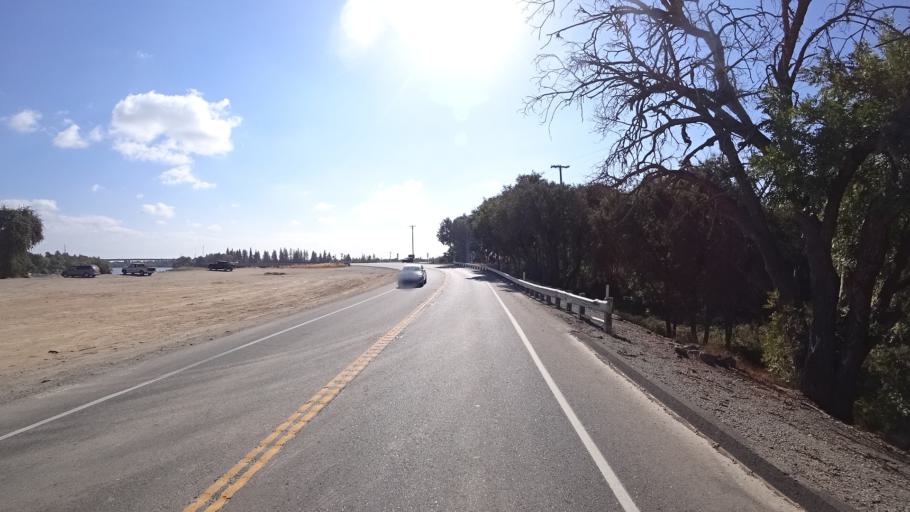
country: US
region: California
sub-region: Yolo County
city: West Sacramento
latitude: 38.6081
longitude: -121.5602
